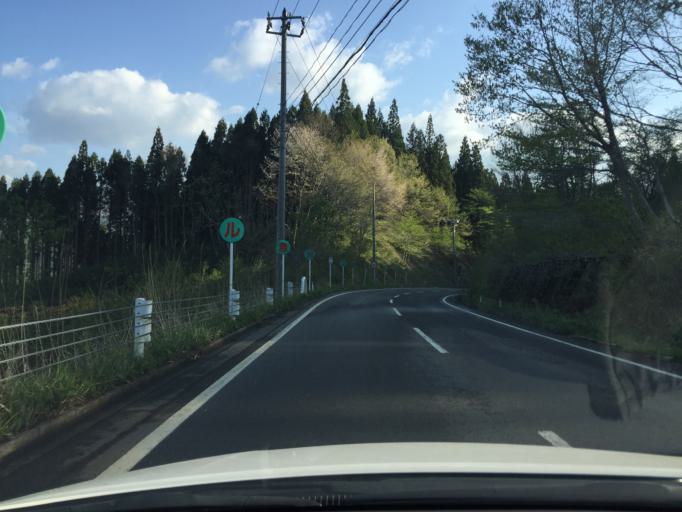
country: JP
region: Fukushima
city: Inawashiro
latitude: 37.6617
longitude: 140.0106
